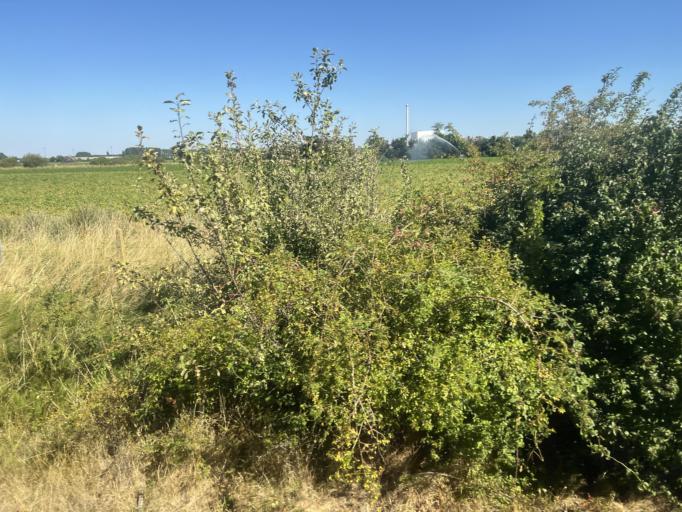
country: GB
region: England
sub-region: Lincolnshire
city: Sleaford
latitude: 52.9939
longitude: -0.3855
